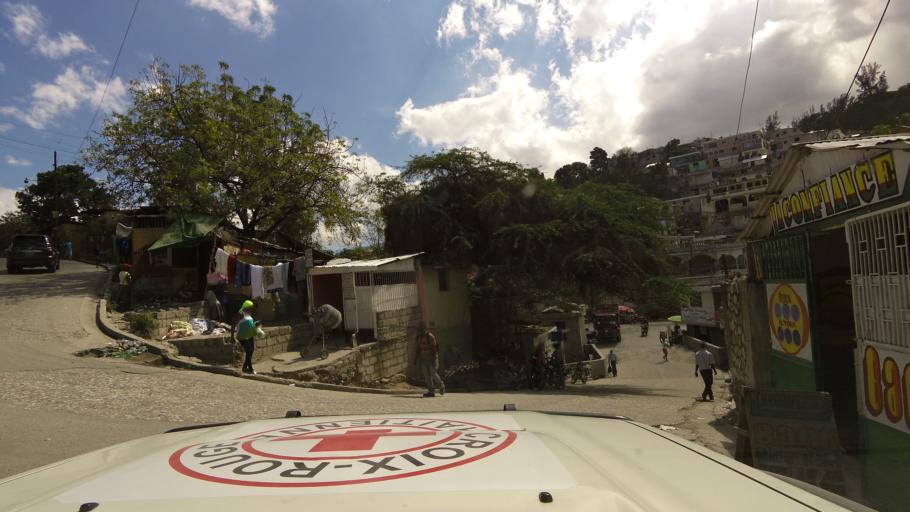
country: HT
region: Ouest
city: Petionville
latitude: 18.5292
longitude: -72.2917
